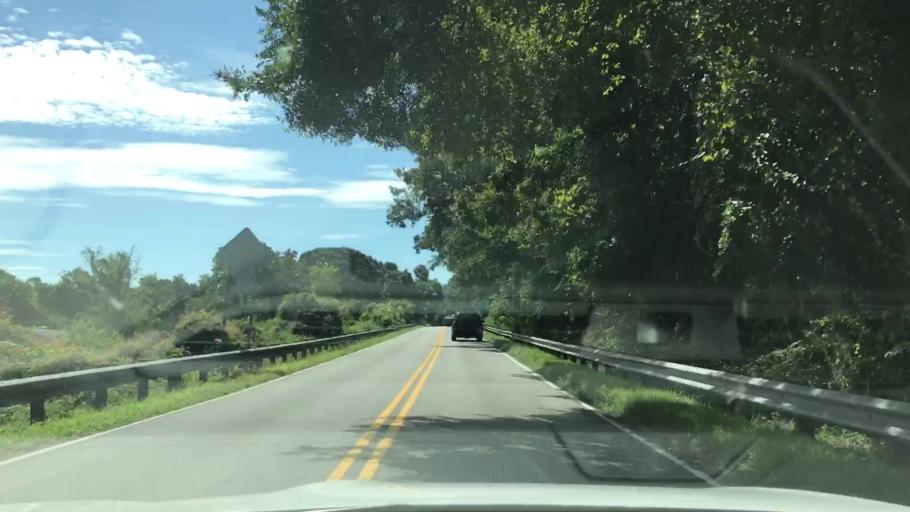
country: US
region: South Carolina
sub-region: Charleston County
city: Shell Point
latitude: 32.8431
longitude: -80.0576
